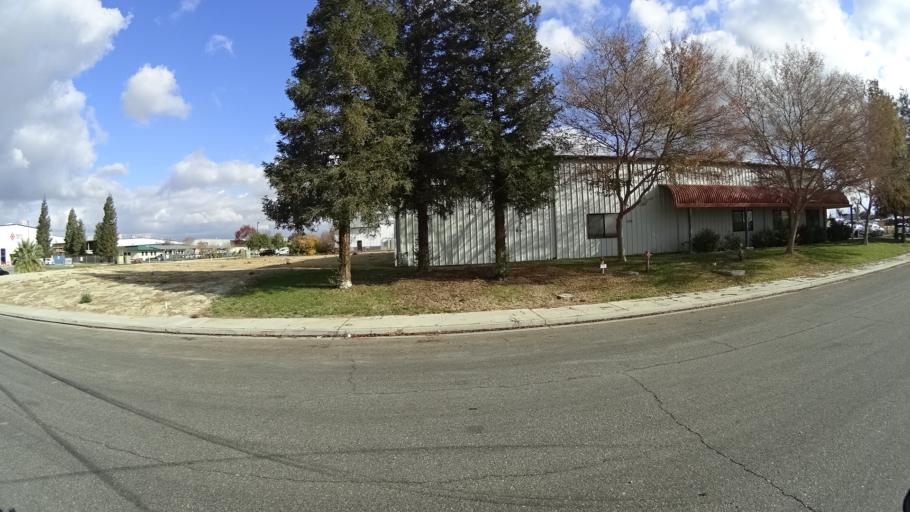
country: US
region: California
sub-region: Kern County
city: Bakersfield
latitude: 35.3493
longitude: -118.9720
